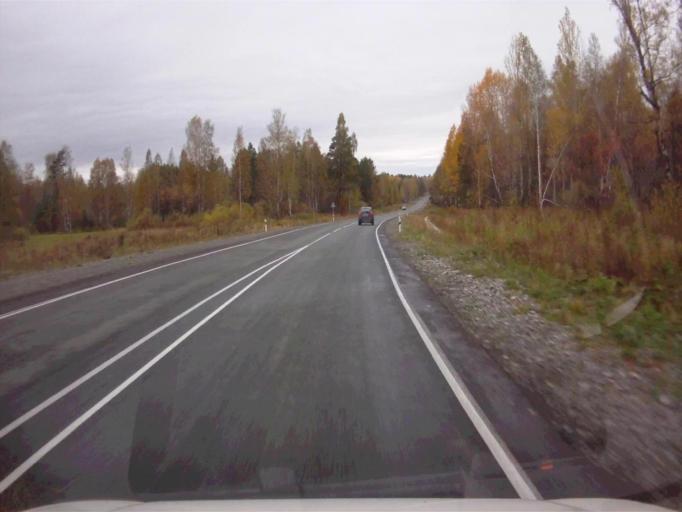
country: RU
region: Chelyabinsk
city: Nyazepetrovsk
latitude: 56.0455
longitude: 59.7557
